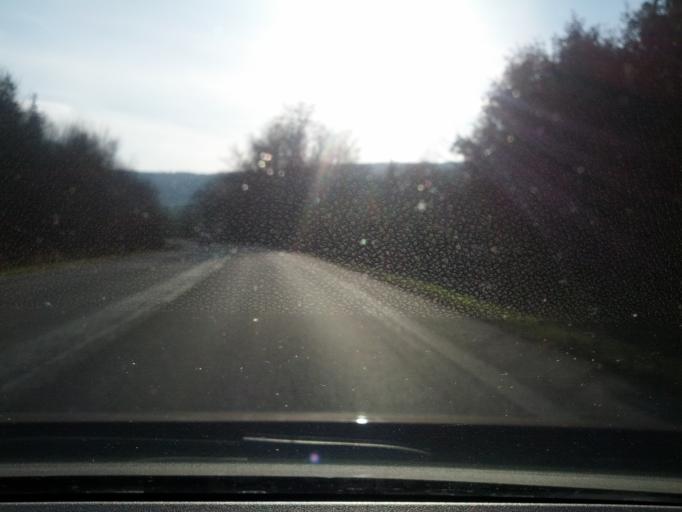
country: DE
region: Lower Saxony
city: Scheden
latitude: 51.4013
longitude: 9.7265
